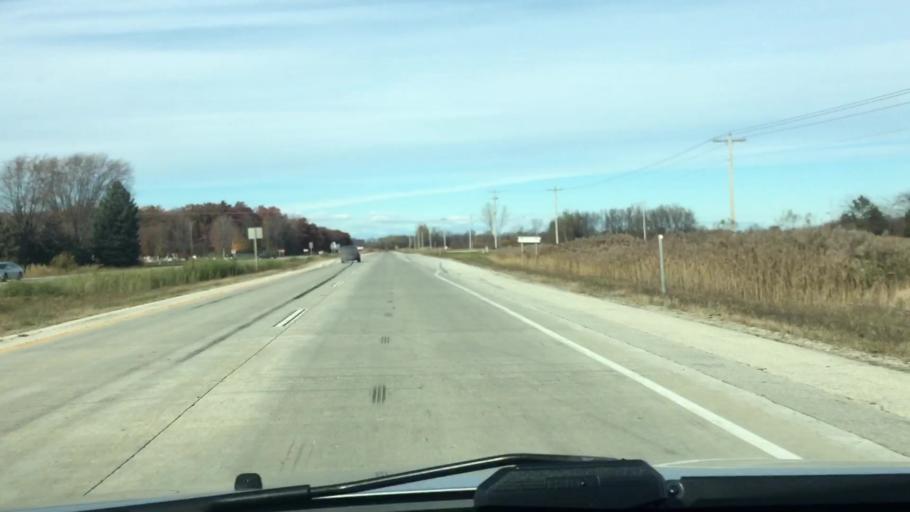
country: US
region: Wisconsin
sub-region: Brown County
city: Bellevue
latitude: 44.5511
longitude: -87.8809
